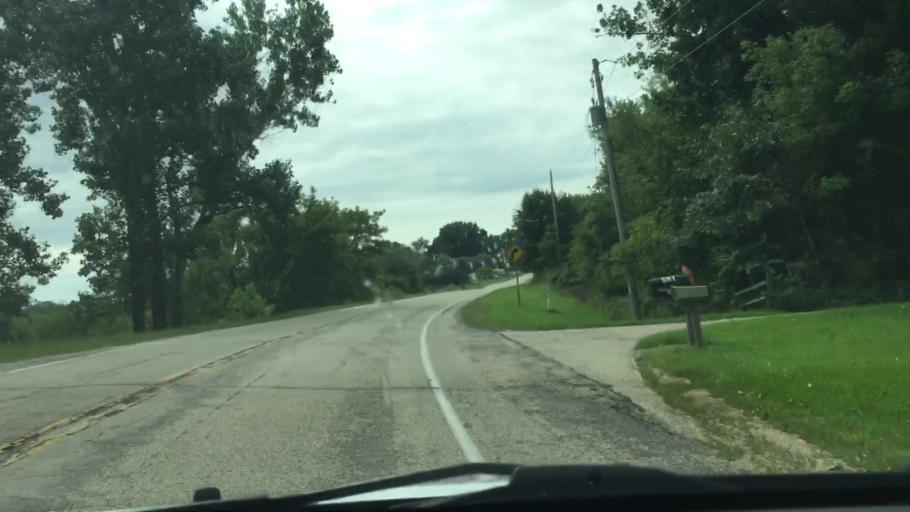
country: US
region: Wisconsin
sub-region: Dane County
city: Belleville
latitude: 42.8855
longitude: -89.4805
